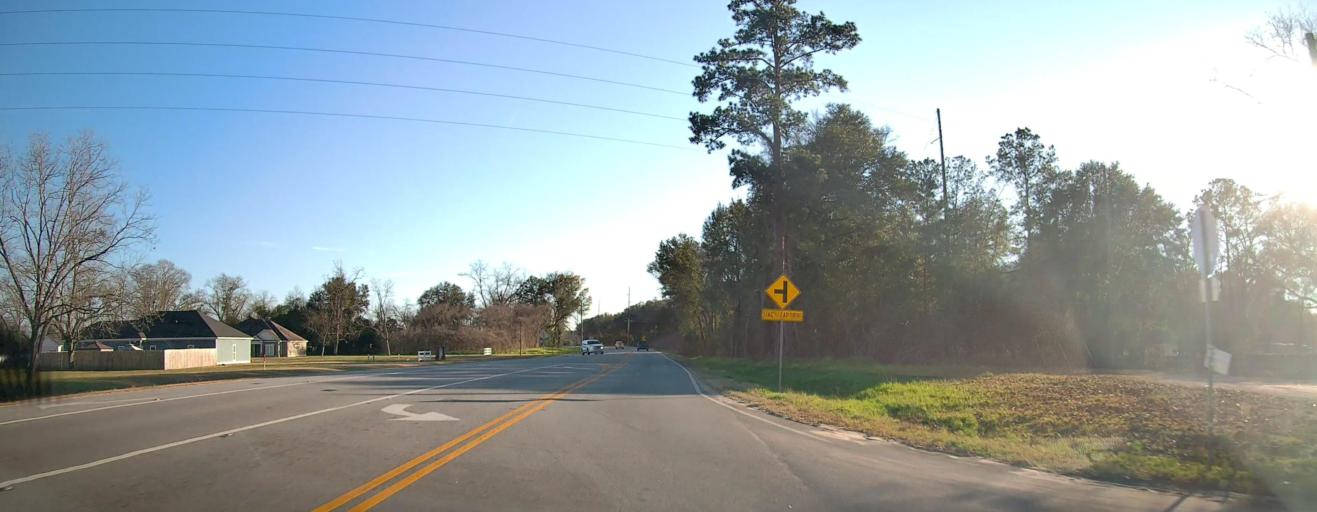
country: US
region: Georgia
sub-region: Dougherty County
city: Albany
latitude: 31.6336
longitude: -84.1628
